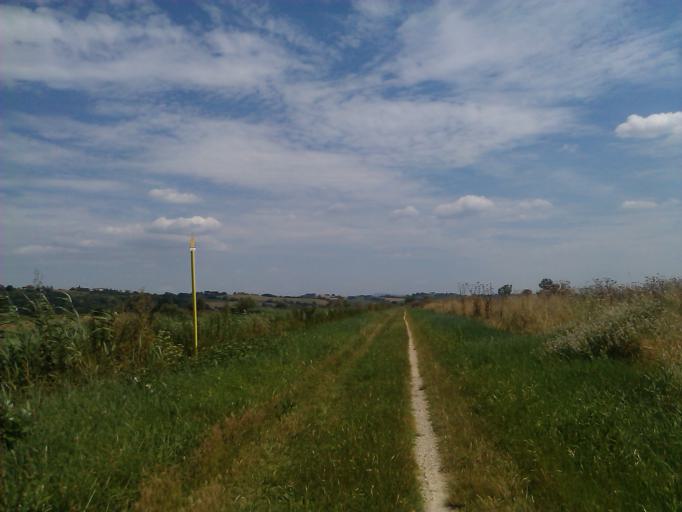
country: IT
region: Tuscany
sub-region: Provincia di Siena
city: Acquaviva
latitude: 43.1251
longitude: 11.9069
